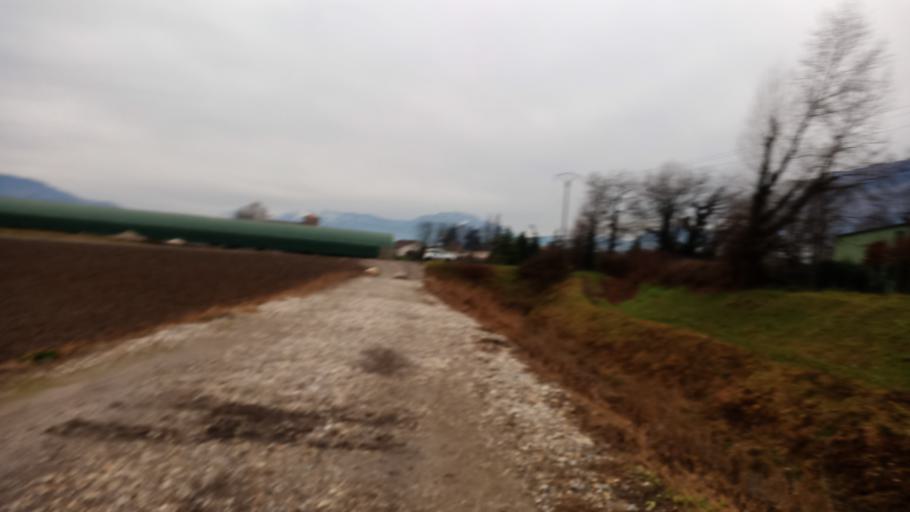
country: FR
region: Rhone-Alpes
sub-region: Departement de l'Isere
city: Saint-Nazaire-les-Eymes
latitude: 45.2407
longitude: 5.8566
